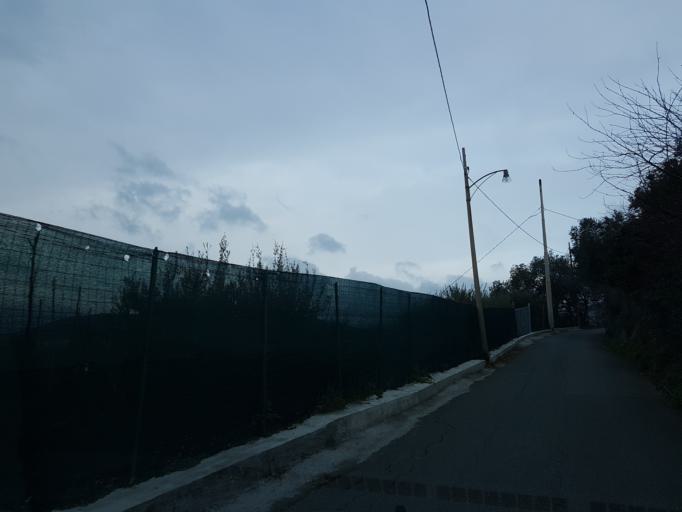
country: IT
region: Liguria
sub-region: Provincia di Genova
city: Mele
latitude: 44.4320
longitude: 8.7966
